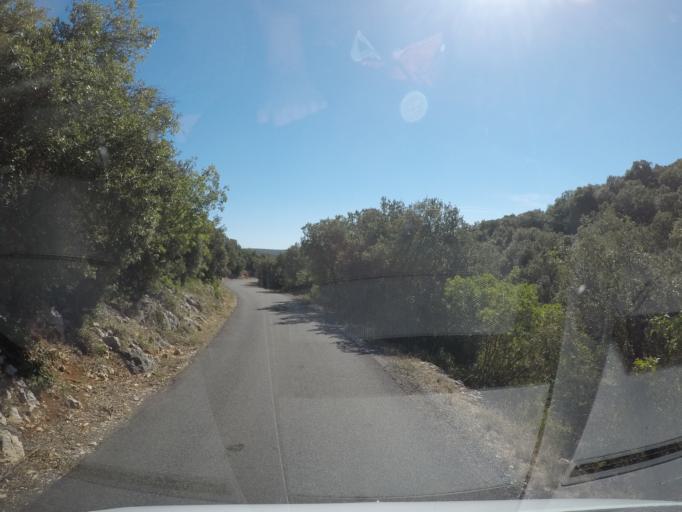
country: FR
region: Languedoc-Roussillon
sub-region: Departement de l'Herault
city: Vailhauques
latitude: 43.7145
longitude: 3.6804
